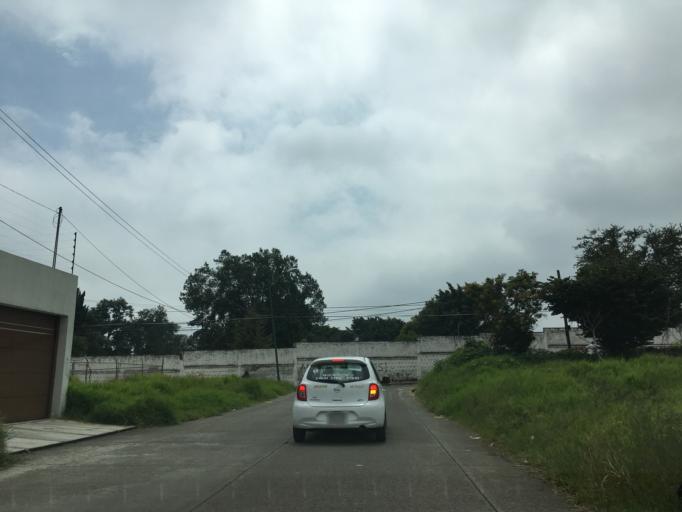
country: MX
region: Michoacan
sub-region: Uruapan
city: Uruapan
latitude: 19.4131
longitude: -102.0688
